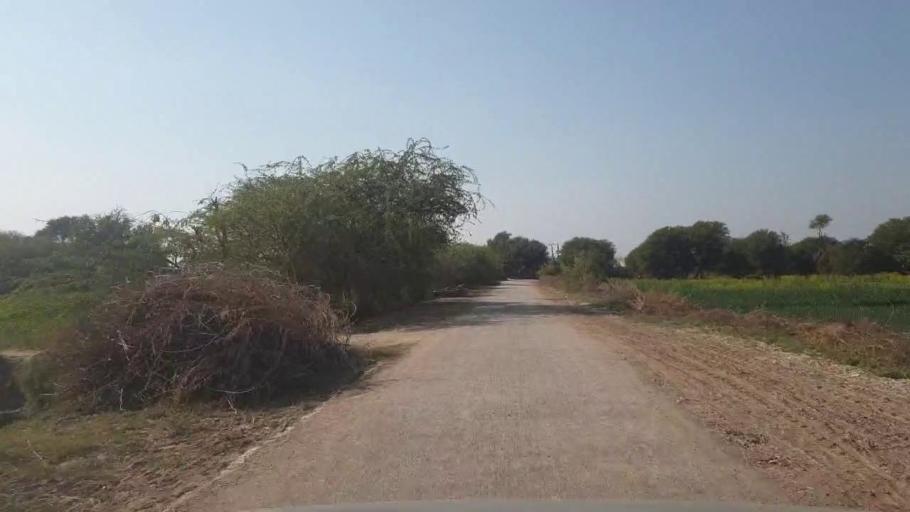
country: PK
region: Sindh
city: Chambar
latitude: 25.3130
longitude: 68.8434
